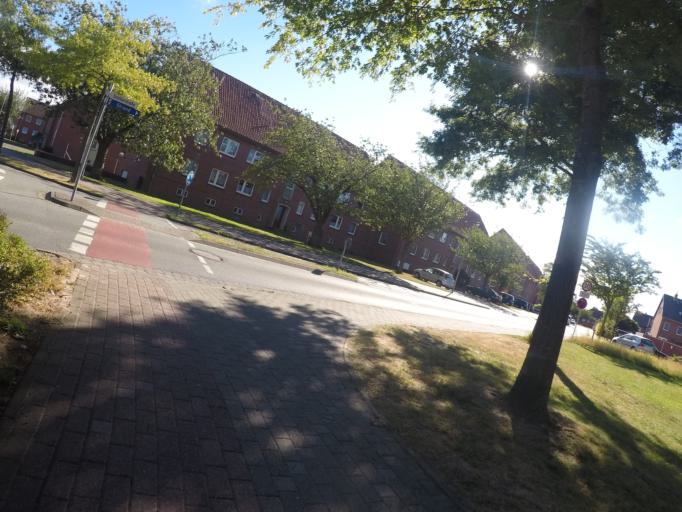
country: DE
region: Lower Saxony
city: Otterndorf
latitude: 53.8119
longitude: 8.9072
